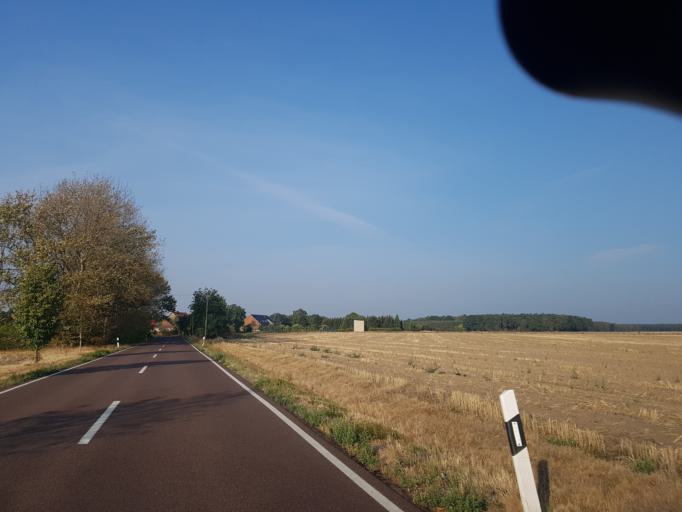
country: DE
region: Saxony-Anhalt
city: Kropstadt
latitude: 51.9839
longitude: 12.6640
